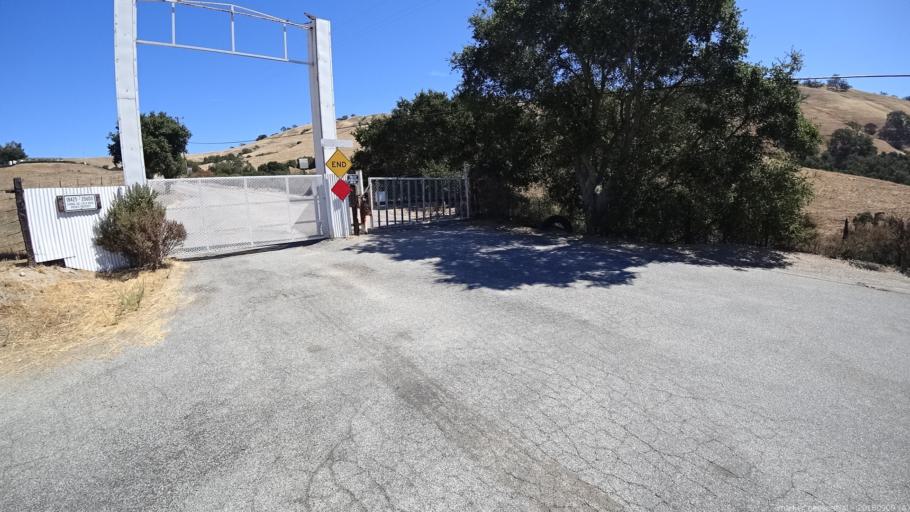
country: US
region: California
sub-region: Monterey County
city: Carmel Valley Village
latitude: 36.5424
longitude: -121.6528
